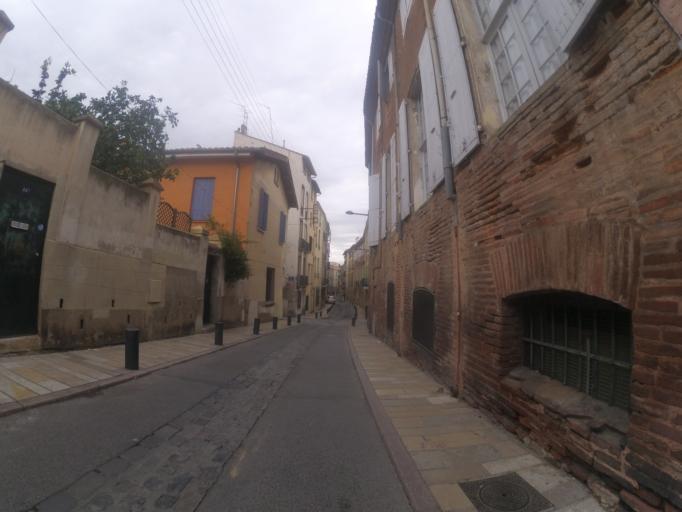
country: FR
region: Languedoc-Roussillon
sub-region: Departement des Pyrenees-Orientales
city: Perpignan
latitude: 42.6964
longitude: 2.8972
